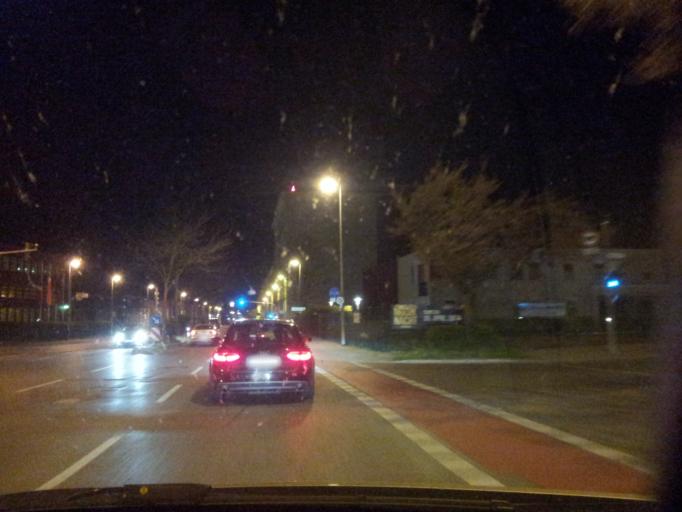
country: DE
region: Baden-Wuerttemberg
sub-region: Regierungsbezirk Stuttgart
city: Goeppingen
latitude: 48.7064
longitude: 9.6417
